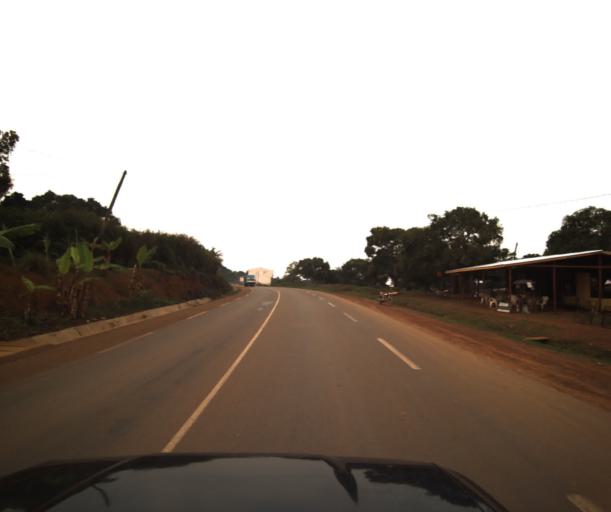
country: CM
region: Centre
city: Mbankomo
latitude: 3.8013
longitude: 11.4592
